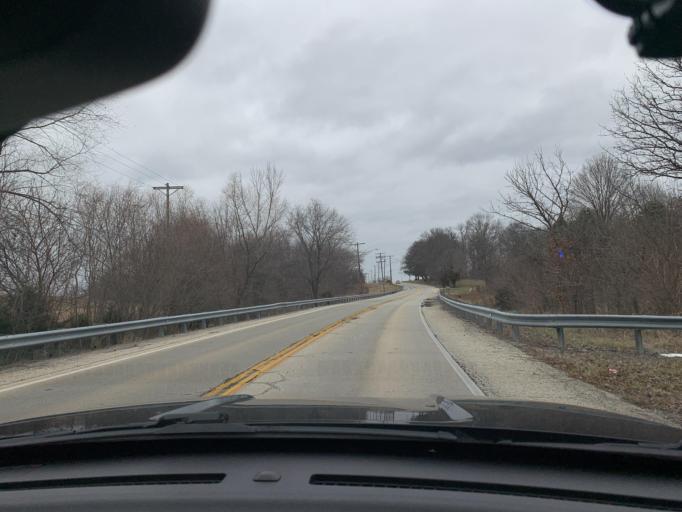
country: US
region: Illinois
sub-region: Sangamon County
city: Jerome
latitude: 39.7293
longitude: -89.6910
